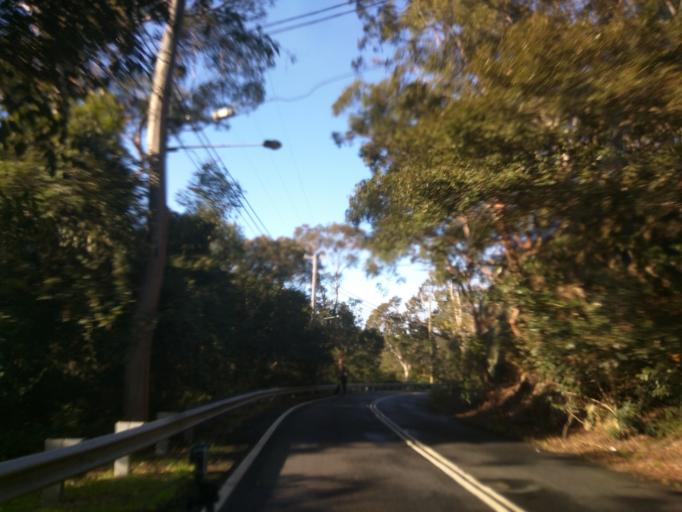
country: AU
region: New South Wales
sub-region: Hurstville
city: Lugarno
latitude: -33.9899
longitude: 151.0450
